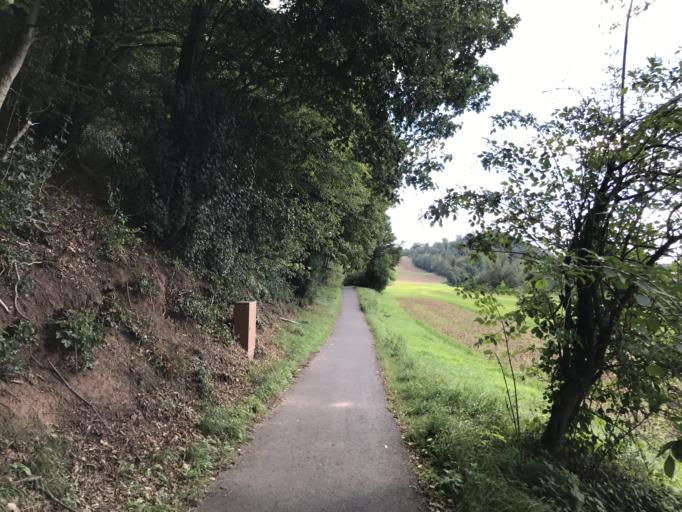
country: DE
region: Hesse
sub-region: Regierungsbezirk Kassel
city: Bad Sooden-Allendorf
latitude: 51.2342
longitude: 10.0013
